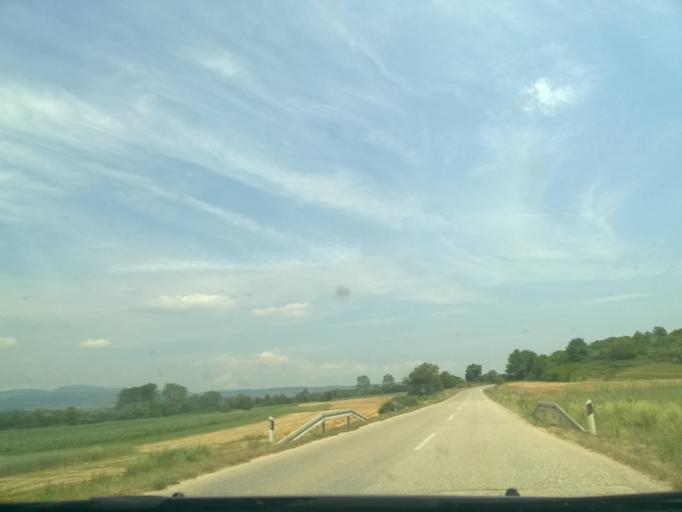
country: RS
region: Central Serbia
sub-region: Zajecarski Okrug
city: Soko Banja
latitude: 43.6544
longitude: 21.7767
